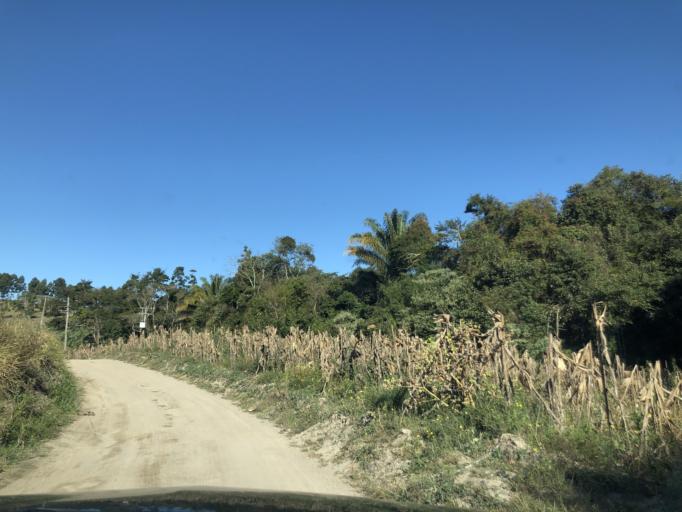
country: BR
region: Sao Paulo
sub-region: Pilar Do Sul
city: Pilar do Sul
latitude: -23.8262
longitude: -47.6280
